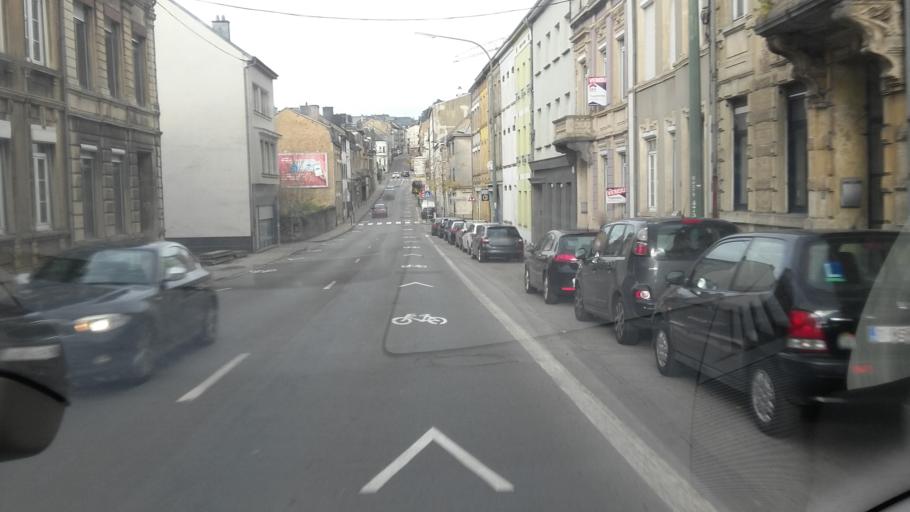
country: BE
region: Wallonia
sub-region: Province du Luxembourg
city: Arlon
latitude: 49.6804
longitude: 5.8200
